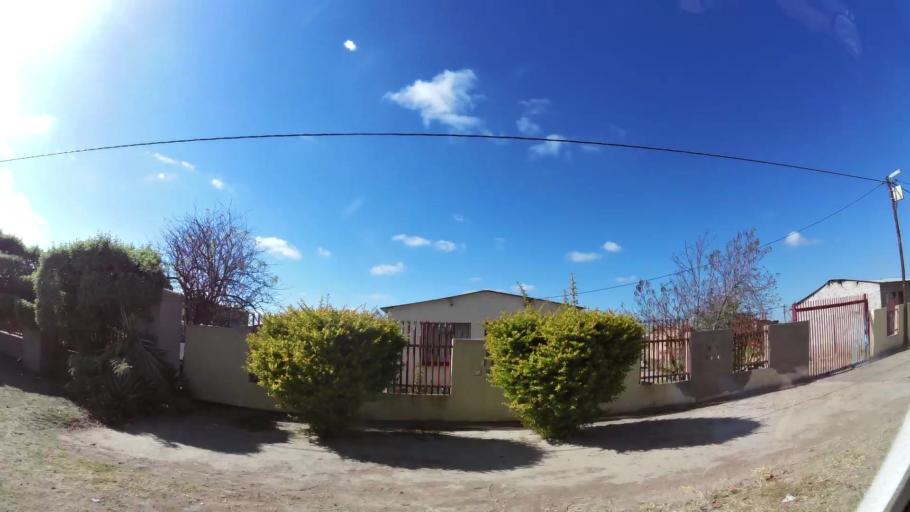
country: ZA
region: Limpopo
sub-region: Capricorn District Municipality
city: Polokwane
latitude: -23.8583
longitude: 29.3985
